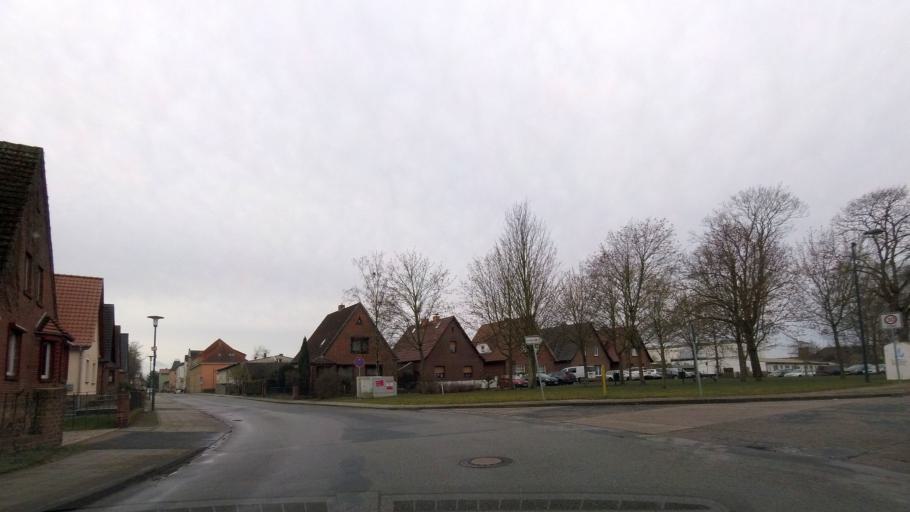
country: DE
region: Mecklenburg-Vorpommern
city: Waren
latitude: 53.5237
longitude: 12.6838
